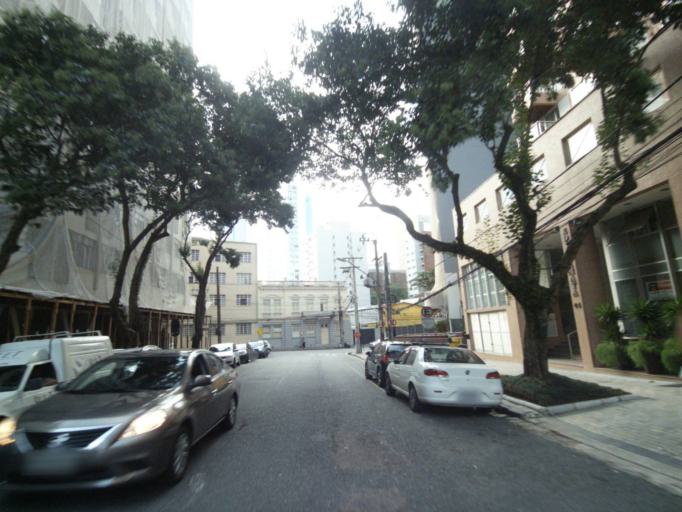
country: BR
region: Parana
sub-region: Curitiba
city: Curitiba
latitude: -25.4371
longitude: -49.2770
